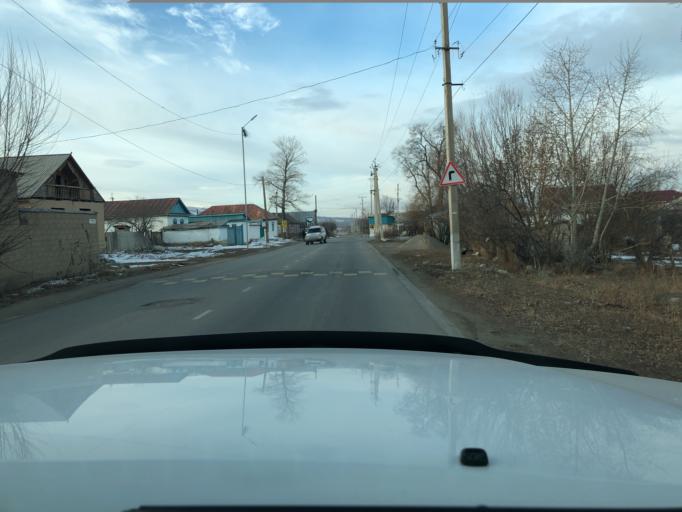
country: KG
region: Ysyk-Koel
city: Karakol
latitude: 42.4682
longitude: 78.3742
